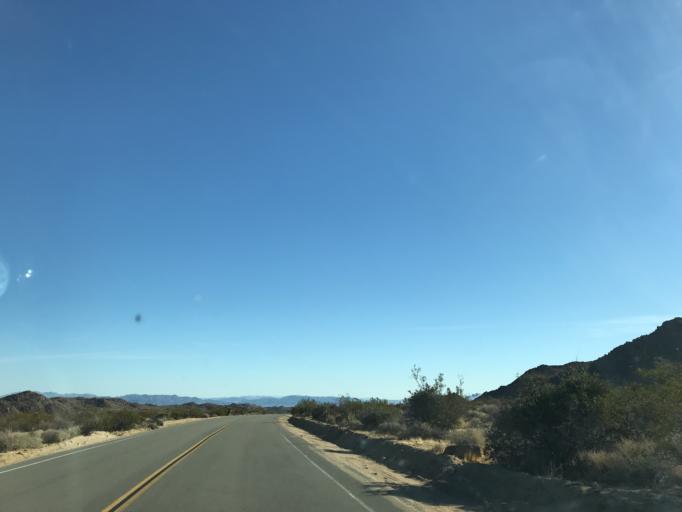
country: US
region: California
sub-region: Riverside County
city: Mecca
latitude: 33.7849
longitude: -115.7954
